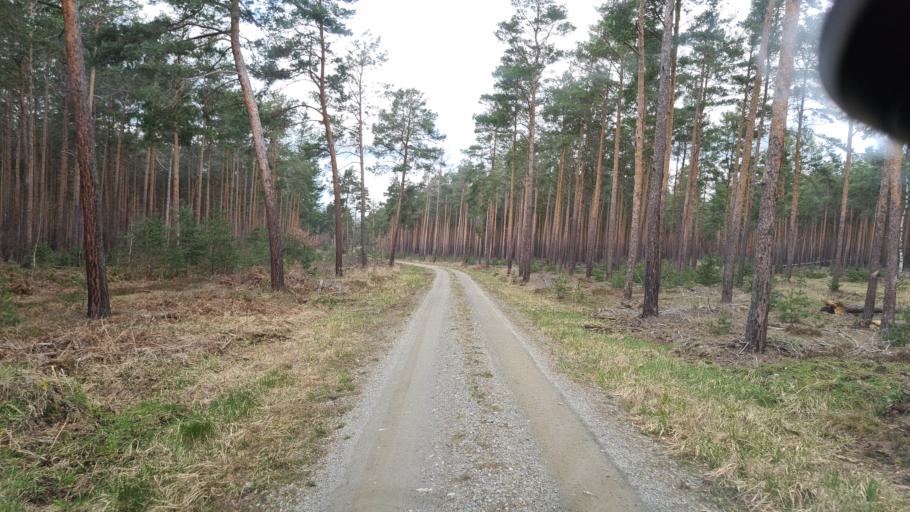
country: DE
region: Brandenburg
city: Schonborn
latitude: 51.6433
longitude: 13.4910
